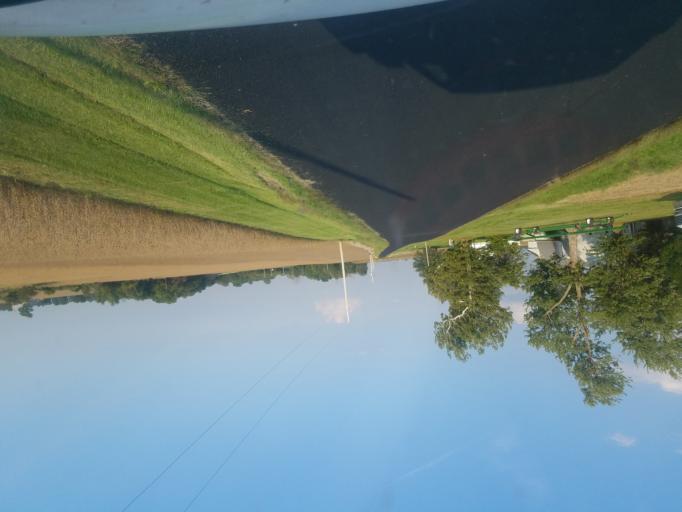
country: US
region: Ohio
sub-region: Crawford County
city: Bucyrus
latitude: 40.9661
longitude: -83.0033
